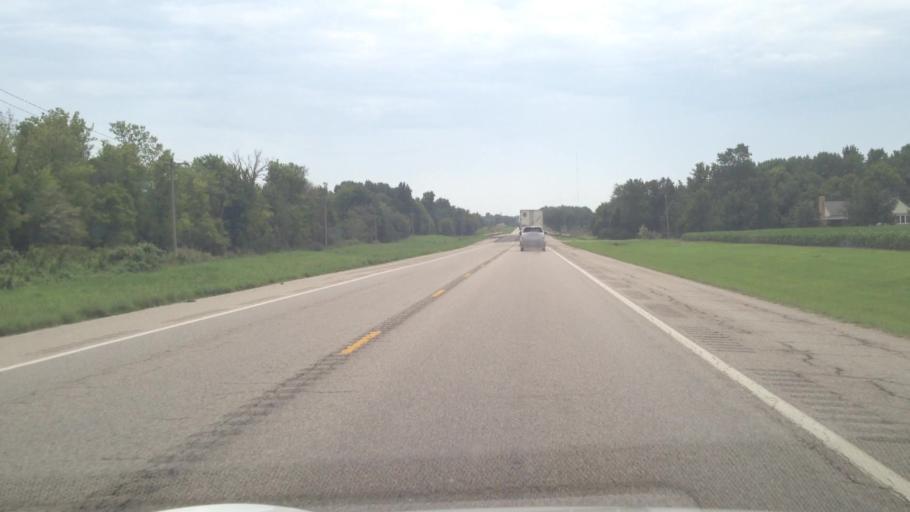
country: US
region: Kansas
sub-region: Crawford County
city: Pittsburg
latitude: 37.2579
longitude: -94.7052
